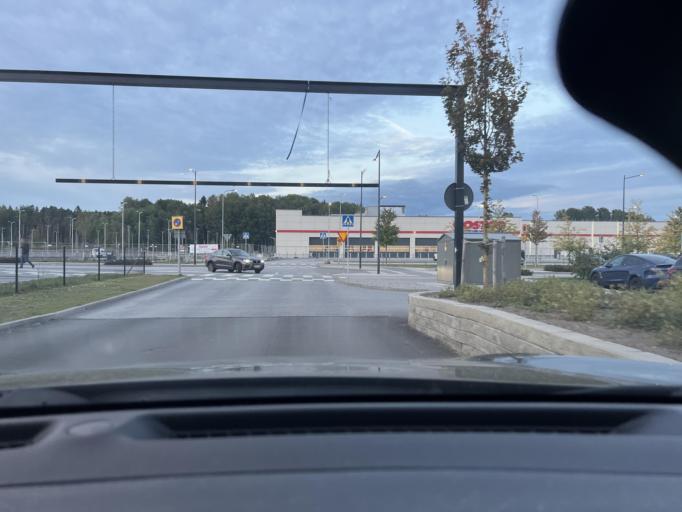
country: SE
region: Stockholm
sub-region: Taby Kommun
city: Taby
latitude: 59.4600
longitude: 18.1369
